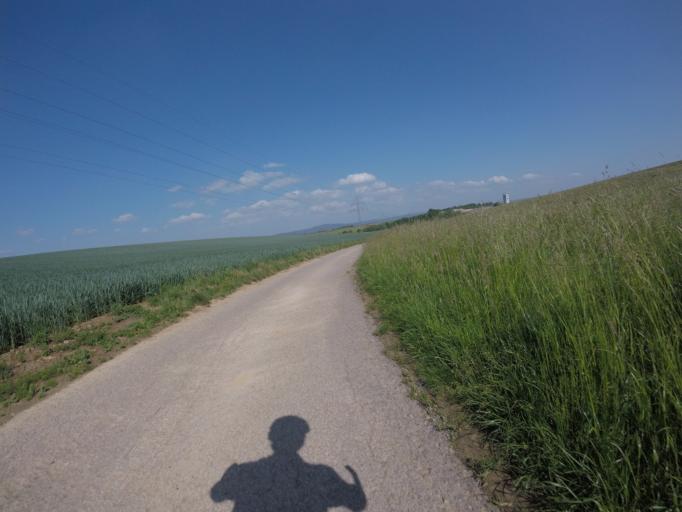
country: DE
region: Baden-Wuerttemberg
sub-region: Regierungsbezirk Stuttgart
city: Kirchberg an der Murr
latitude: 48.9610
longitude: 9.3661
